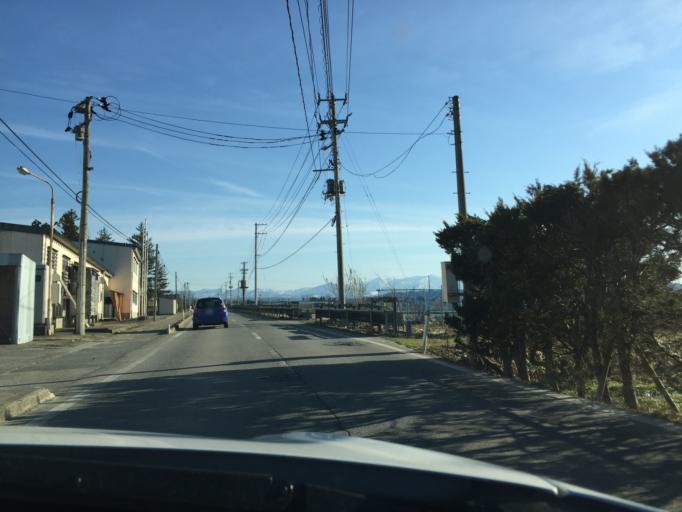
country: JP
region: Yamagata
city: Nagai
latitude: 38.0204
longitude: 140.0559
